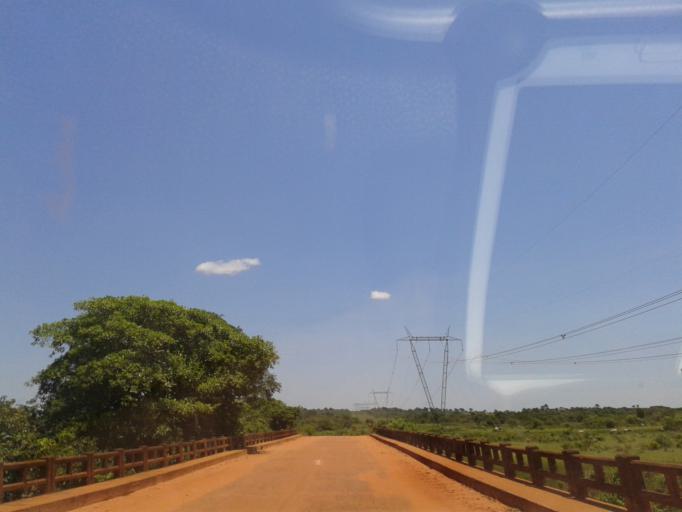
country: BR
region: Minas Gerais
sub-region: Santa Vitoria
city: Santa Vitoria
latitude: -19.2290
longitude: -50.3822
